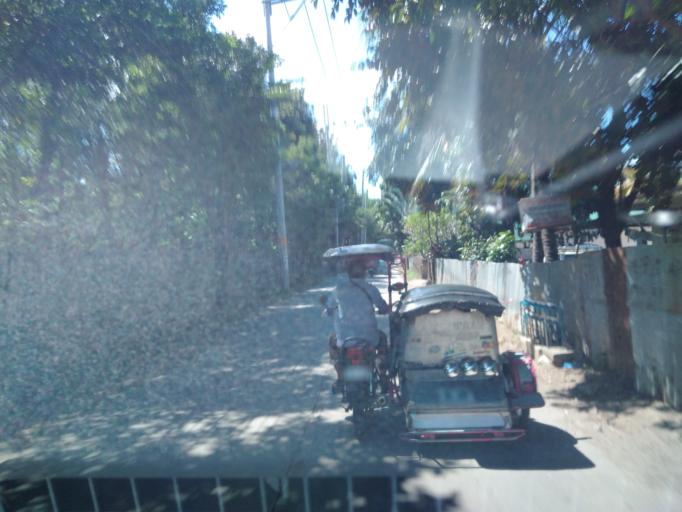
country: PH
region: Central Luzon
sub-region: Province of Bulacan
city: Balasing
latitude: 14.8541
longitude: 121.0123
